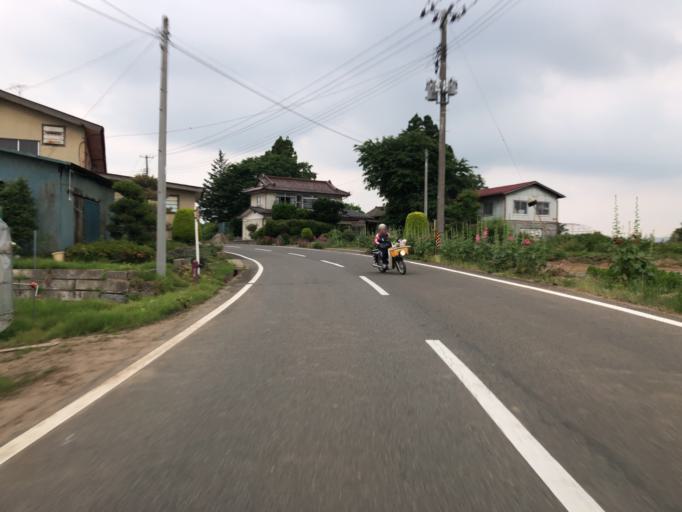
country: JP
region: Fukushima
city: Nihommatsu
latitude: 37.6405
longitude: 140.4792
